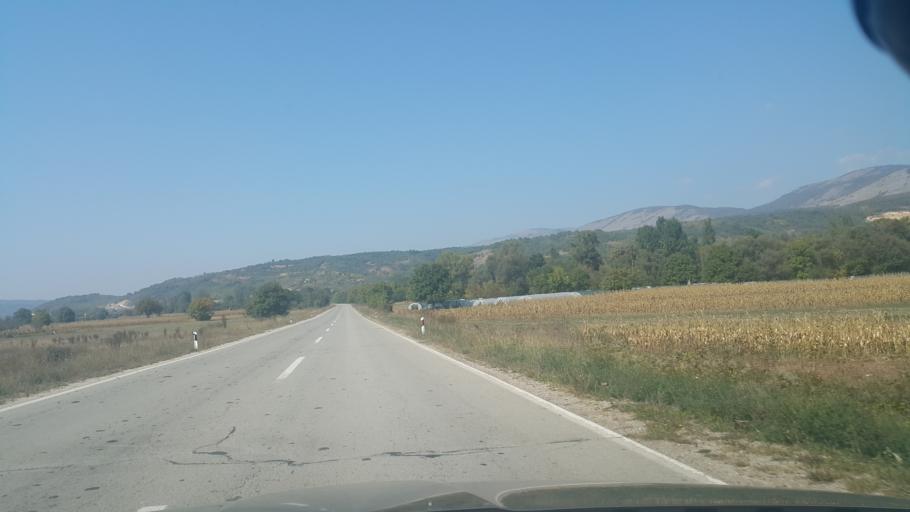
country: RS
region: Central Serbia
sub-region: Pirotski Okrug
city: Bela Palanka
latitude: 43.2251
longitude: 22.3316
